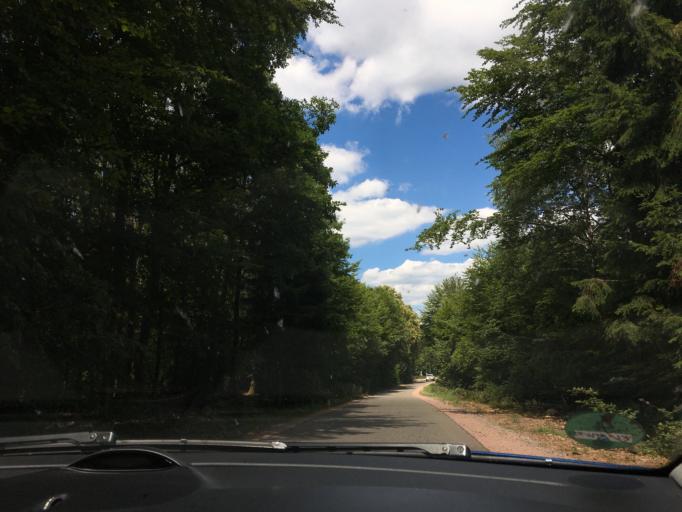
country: DE
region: Rheinland-Pfalz
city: Leimen
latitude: 49.2567
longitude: 7.8280
